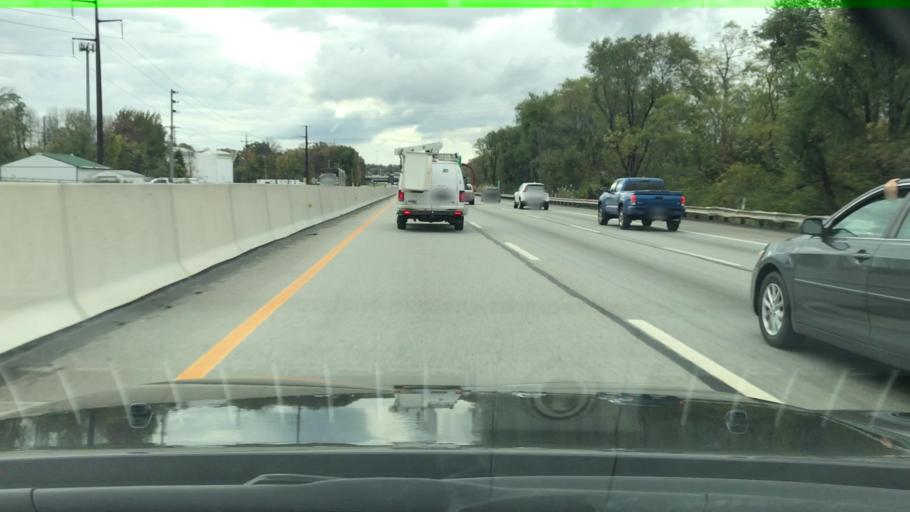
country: US
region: Pennsylvania
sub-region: Montgomery County
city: Hatboro
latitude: 40.1627
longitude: -75.1117
